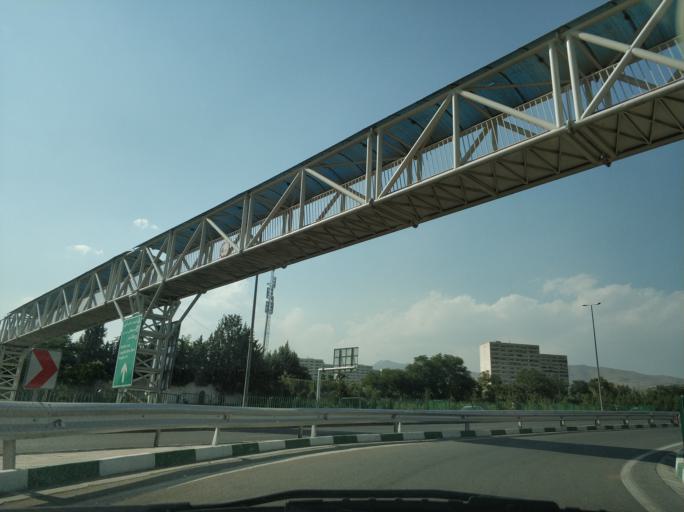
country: IR
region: Tehran
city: Tajrish
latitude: 35.7595
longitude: 51.5365
